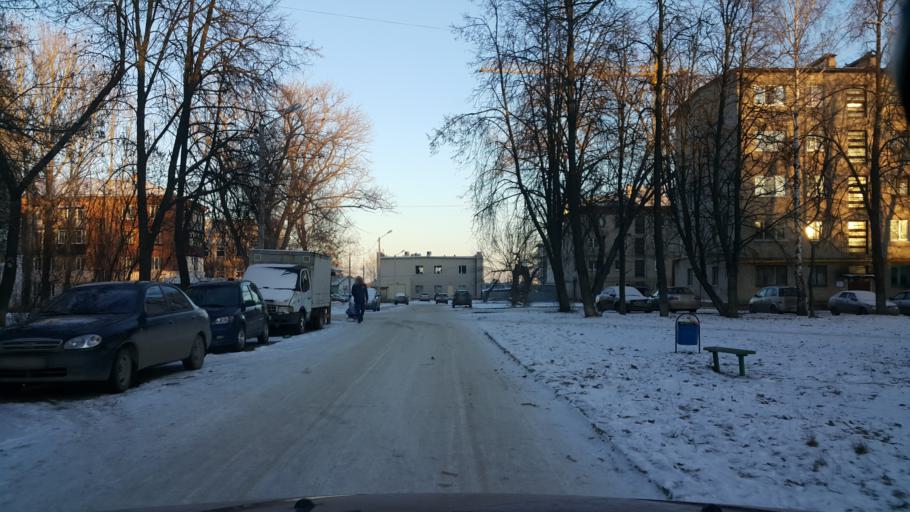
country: RU
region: Tambov
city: Pokrovo-Prigorodnoye
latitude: 52.7085
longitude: 41.3946
